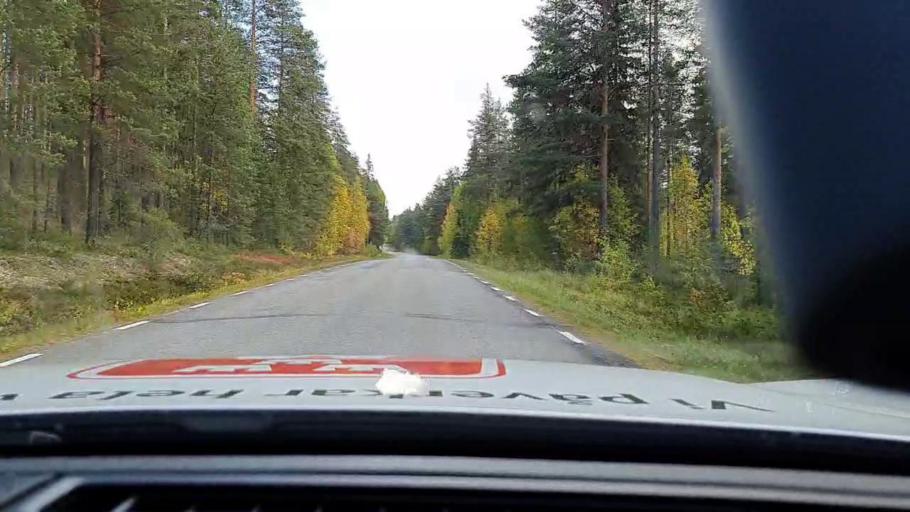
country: SE
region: Vaesterbotten
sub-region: Skelleftea Kommun
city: Langsele
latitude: 64.9435
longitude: 19.9567
